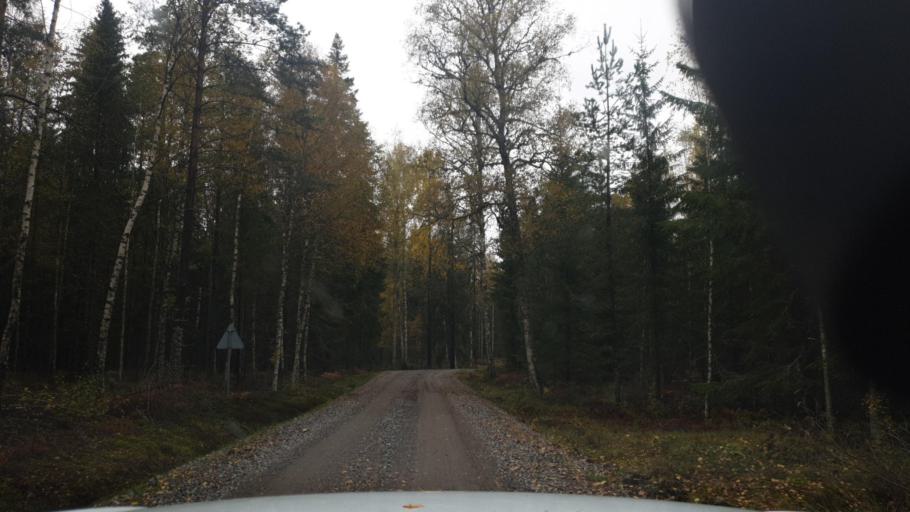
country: SE
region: Vaermland
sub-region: Karlstads Kommun
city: Valberg
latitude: 59.4527
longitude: 13.0943
